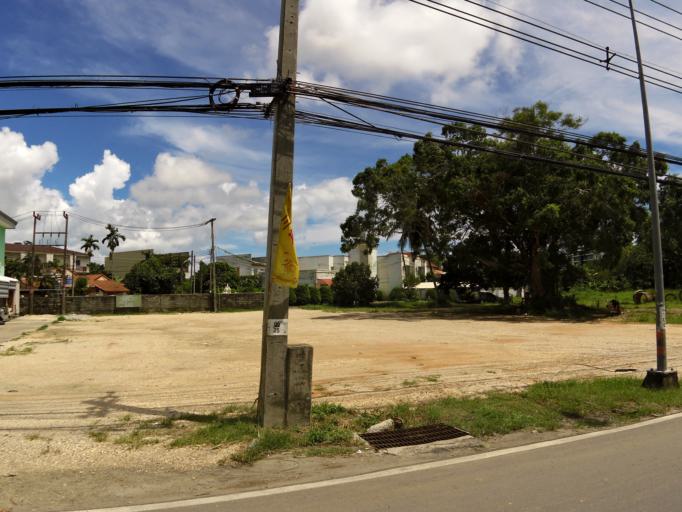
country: TH
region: Phuket
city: Ban Chalong
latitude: 7.8572
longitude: 98.3390
